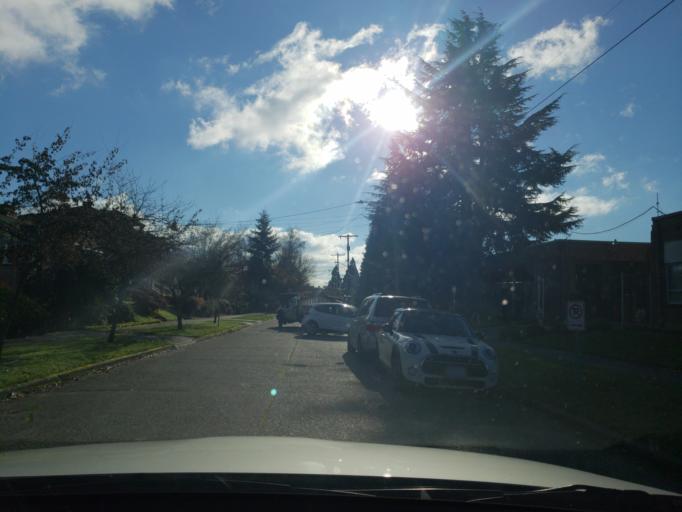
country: US
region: Washington
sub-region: King County
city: Shoreline
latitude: 47.6887
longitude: -122.3378
